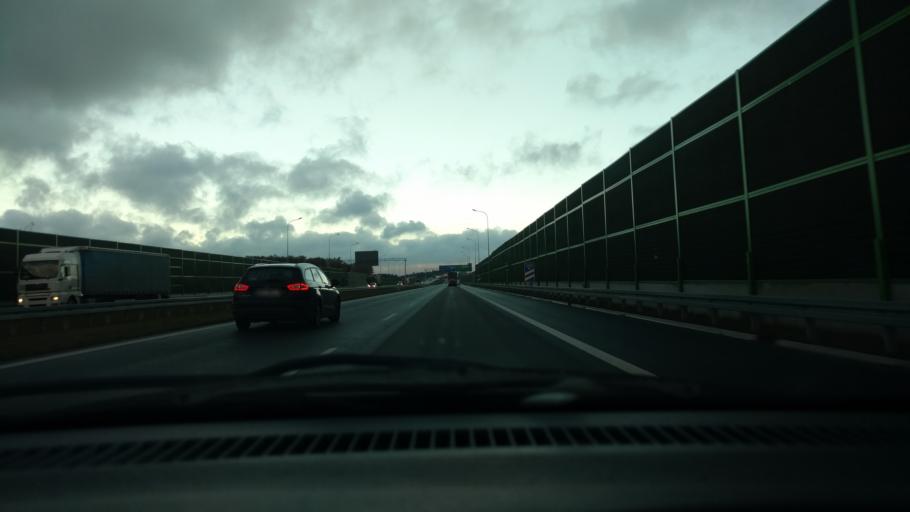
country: PL
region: Lodz Voivodeship
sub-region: Powiat lodzki wschodni
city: Andrespol
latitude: 51.7393
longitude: 19.6009
